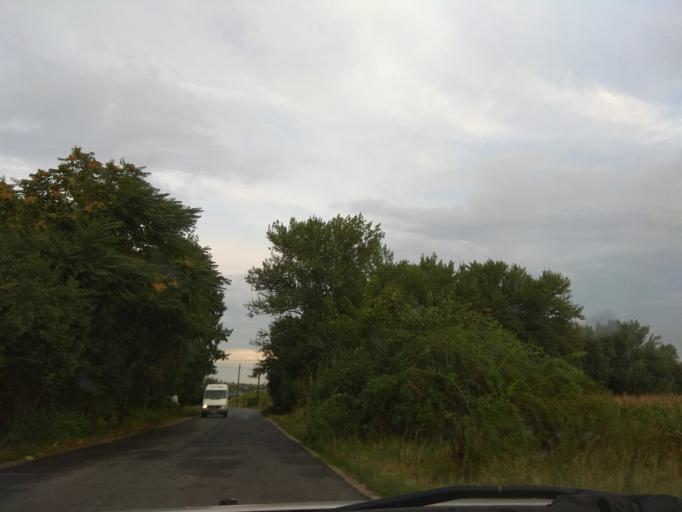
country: HU
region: Borsod-Abauj-Zemplen
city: Felsozsolca
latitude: 48.0865
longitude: 20.8457
